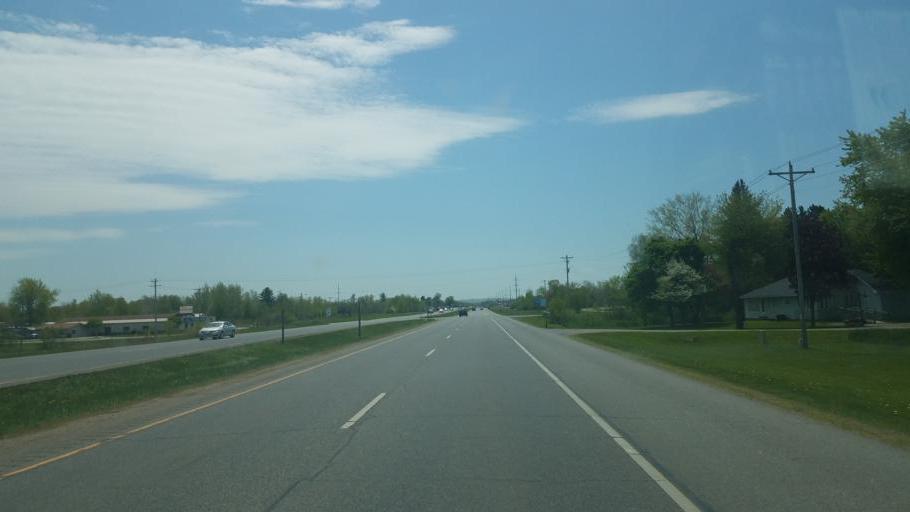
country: US
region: Wisconsin
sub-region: Monroe County
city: Tomah
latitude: 44.0154
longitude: -90.5053
